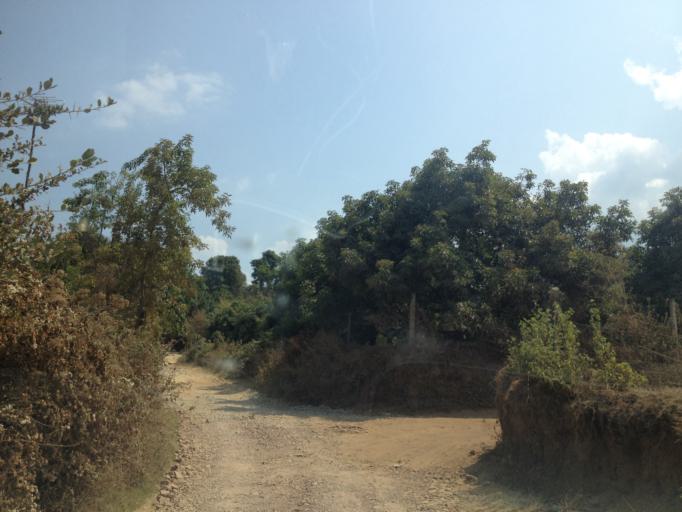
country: MX
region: Michoacan
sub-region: Zitacuaro
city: Macutzio
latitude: 19.4968
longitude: -100.3304
